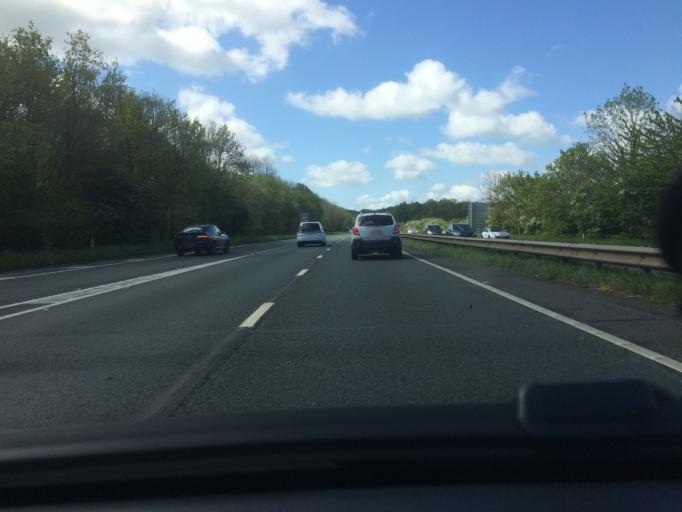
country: GB
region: Wales
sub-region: Wrexham
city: Rossett
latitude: 53.1030
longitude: -2.9595
